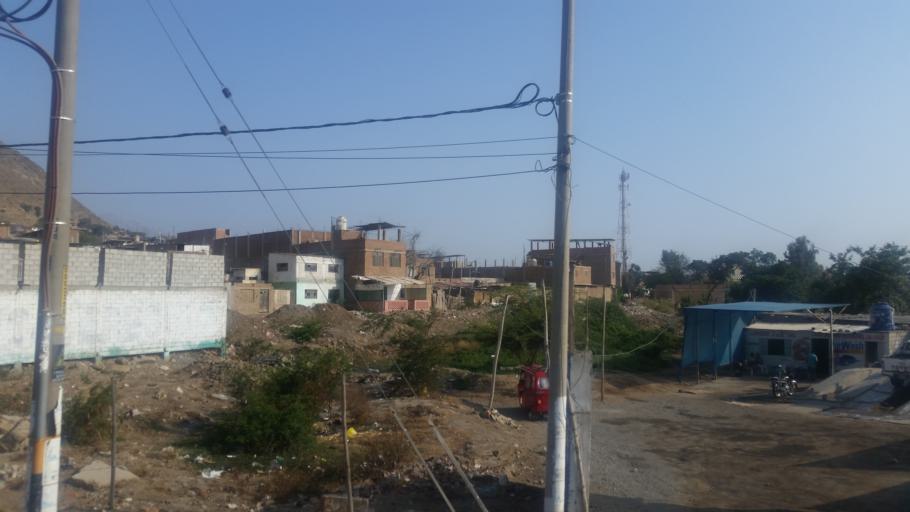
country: PE
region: La Libertad
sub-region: Chepen
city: Chepen
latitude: -7.2192
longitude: -79.4330
